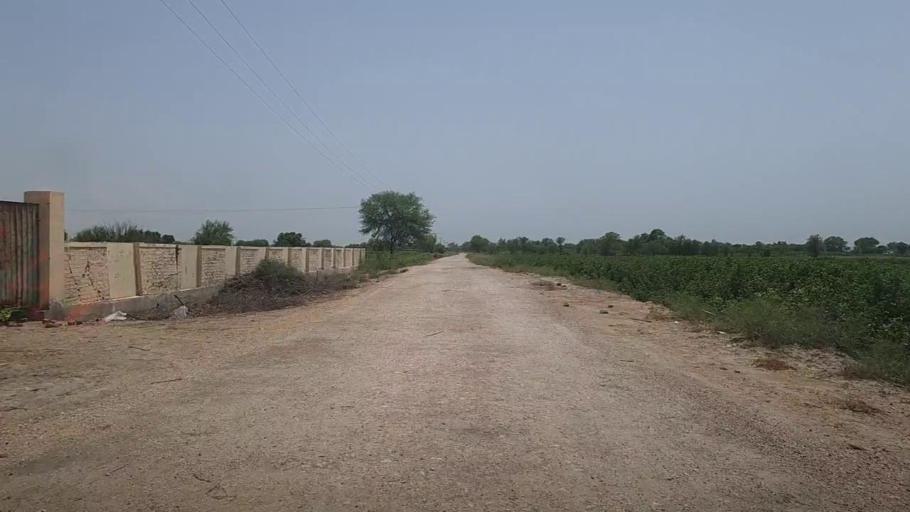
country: PK
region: Sindh
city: Pad Idan
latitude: 26.8393
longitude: 68.3248
